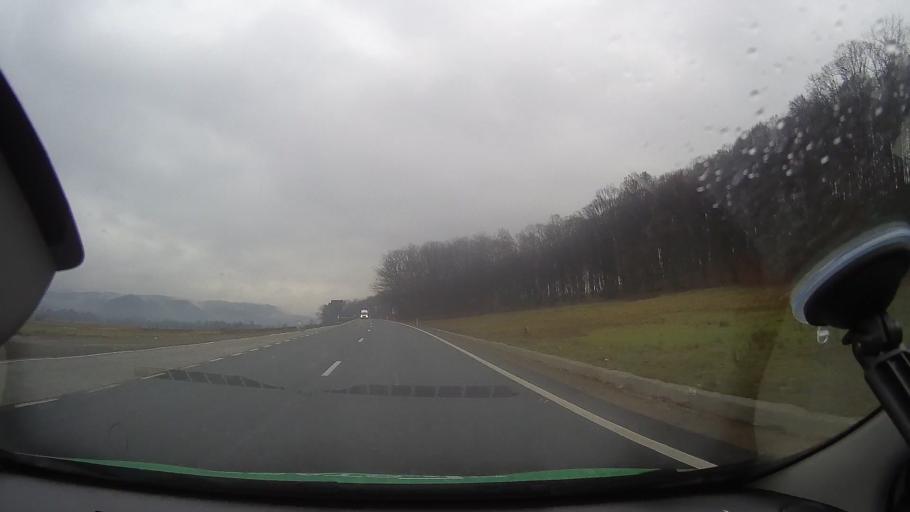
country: RO
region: Hunedoara
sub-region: Comuna Baia de Cris
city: Baia de Cris
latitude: 46.1771
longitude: 22.6924
